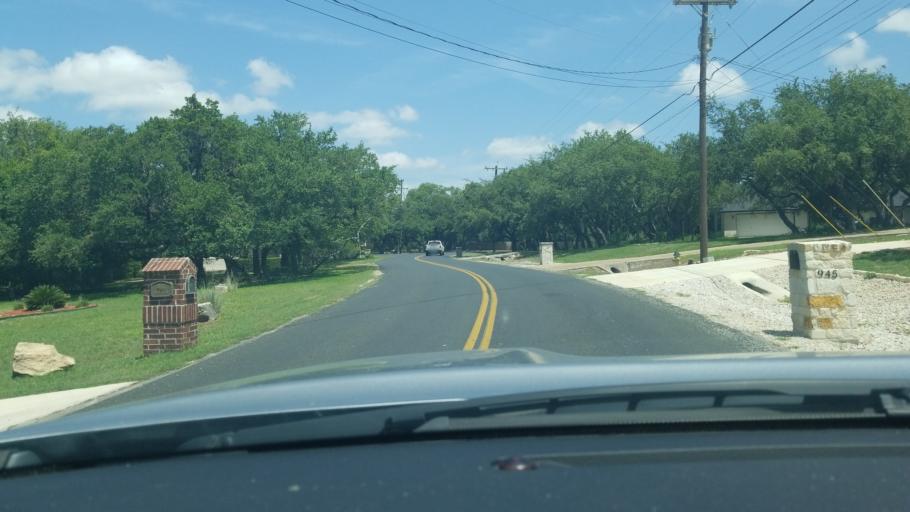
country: US
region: Texas
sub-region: Bexar County
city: Timberwood Park
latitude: 29.6873
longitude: -98.4802
